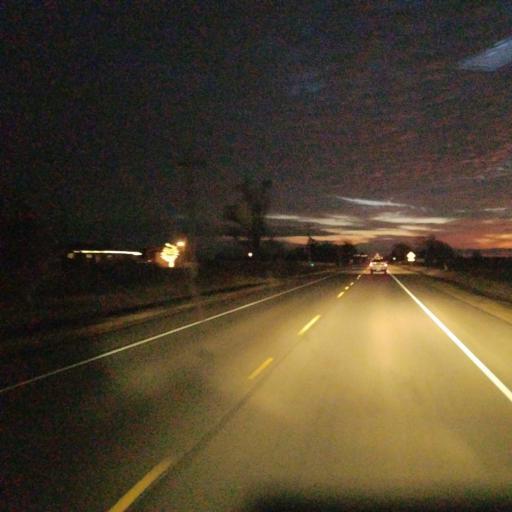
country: US
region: Illinois
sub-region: Peoria County
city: Hanna City
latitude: 40.6974
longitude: -89.8555
